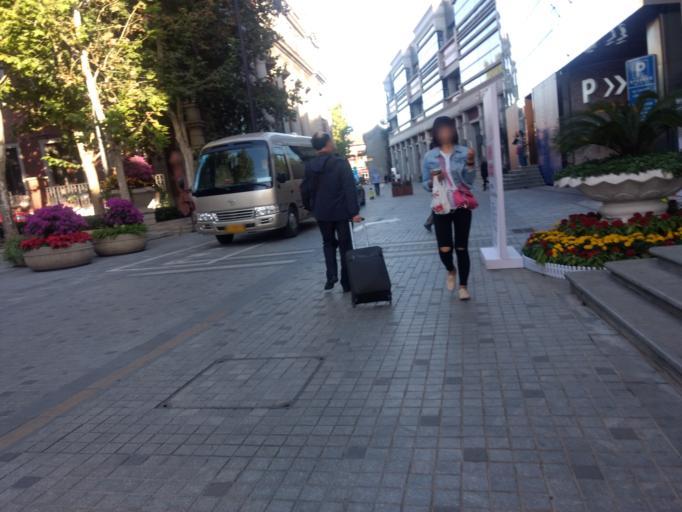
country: CN
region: Beijing
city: Beijing
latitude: 39.8970
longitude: 116.3902
